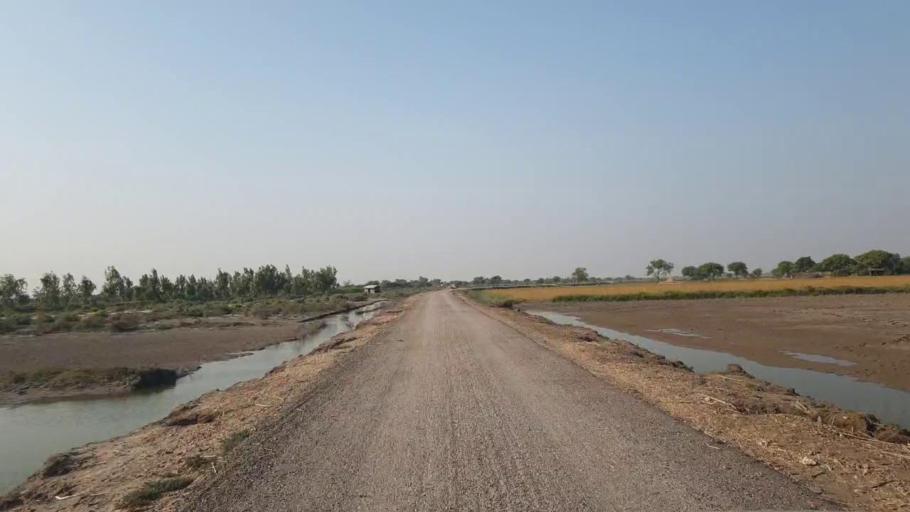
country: PK
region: Sindh
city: Kario
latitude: 24.9003
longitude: 68.6221
